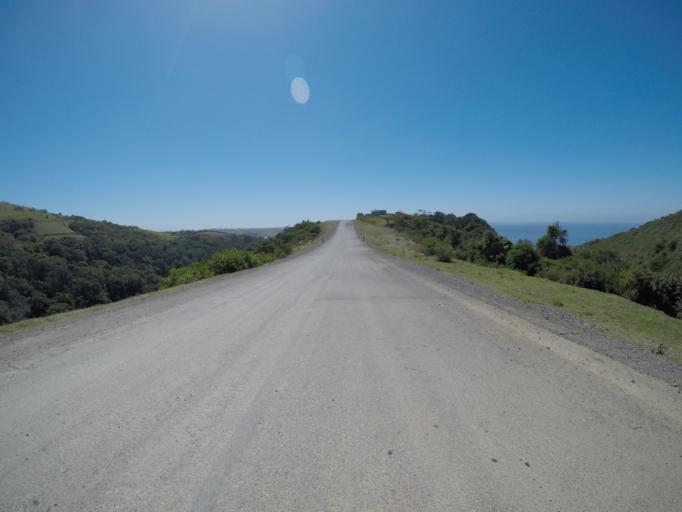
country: ZA
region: Eastern Cape
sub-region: OR Tambo District Municipality
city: Libode
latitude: -31.9940
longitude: 29.1310
